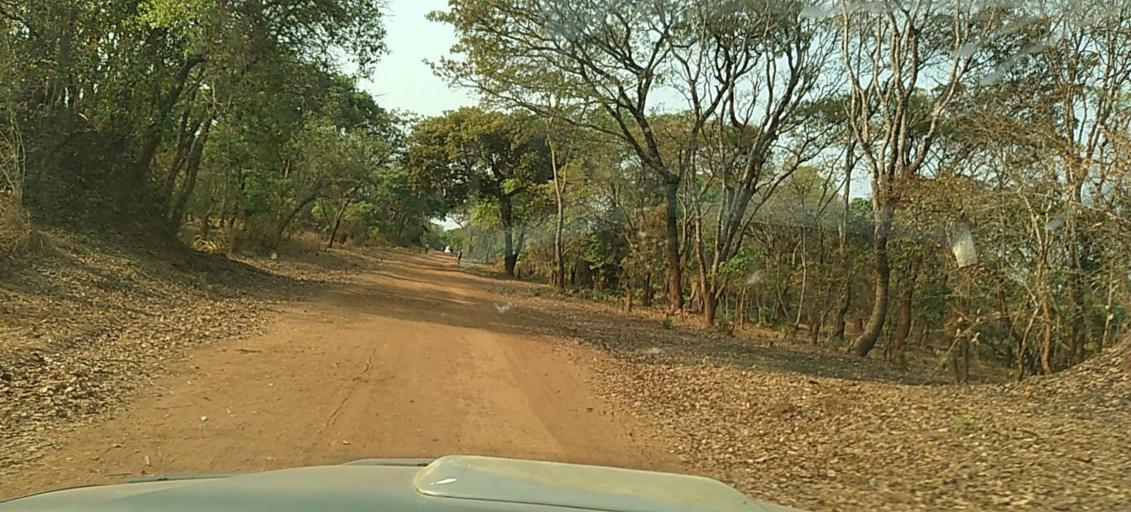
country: ZM
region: North-Western
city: Kasempa
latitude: -13.3106
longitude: 26.5524
